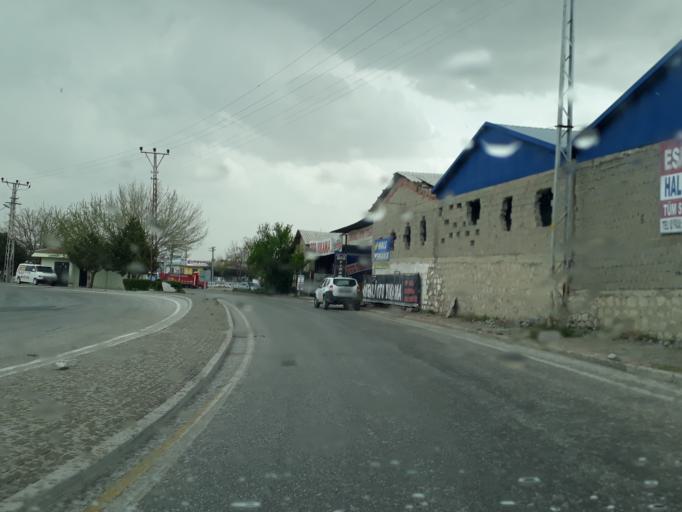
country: TR
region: Konya
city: Selcuklu
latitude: 37.9167
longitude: 32.4757
